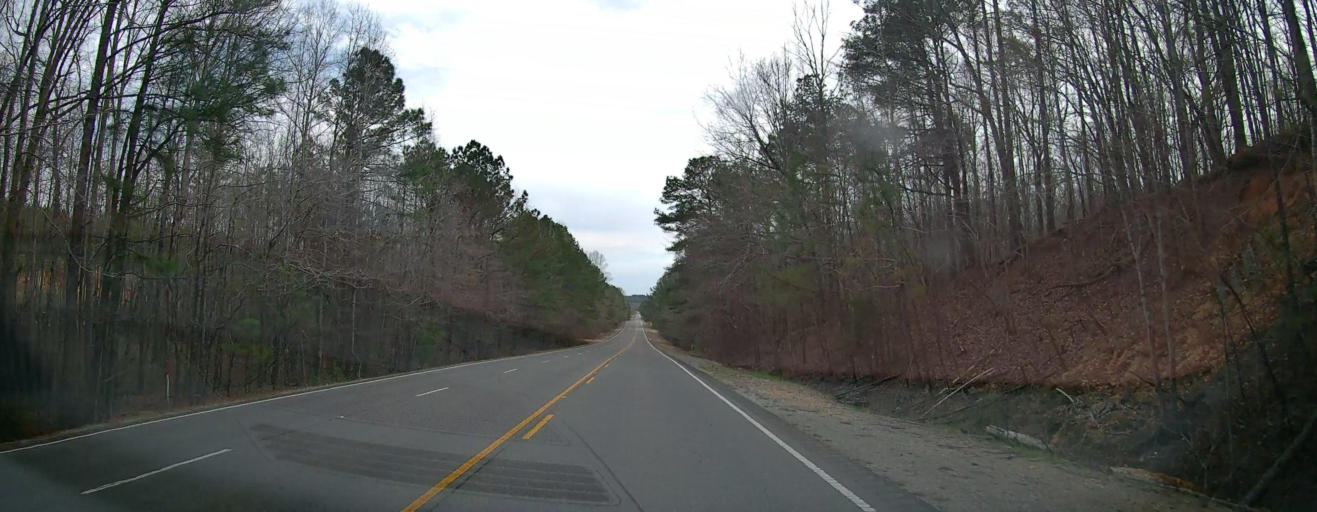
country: US
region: Alabama
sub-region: Marion County
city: Guin
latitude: 34.0215
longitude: -87.9390
